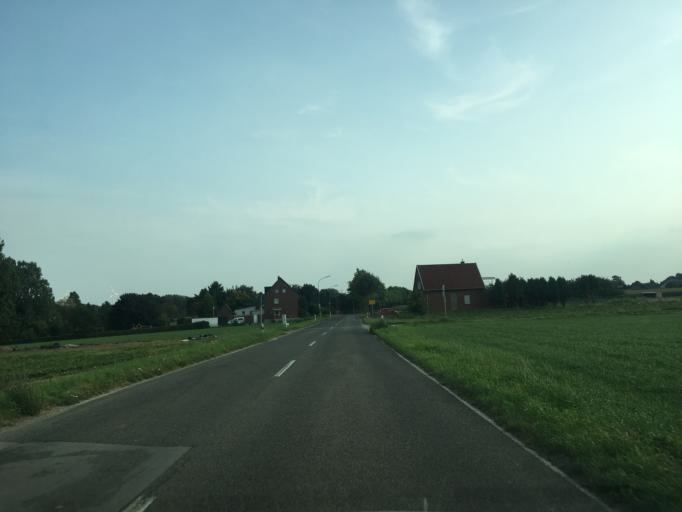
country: DE
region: North Rhine-Westphalia
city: Huckelhoven
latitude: 51.0831
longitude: 6.2252
